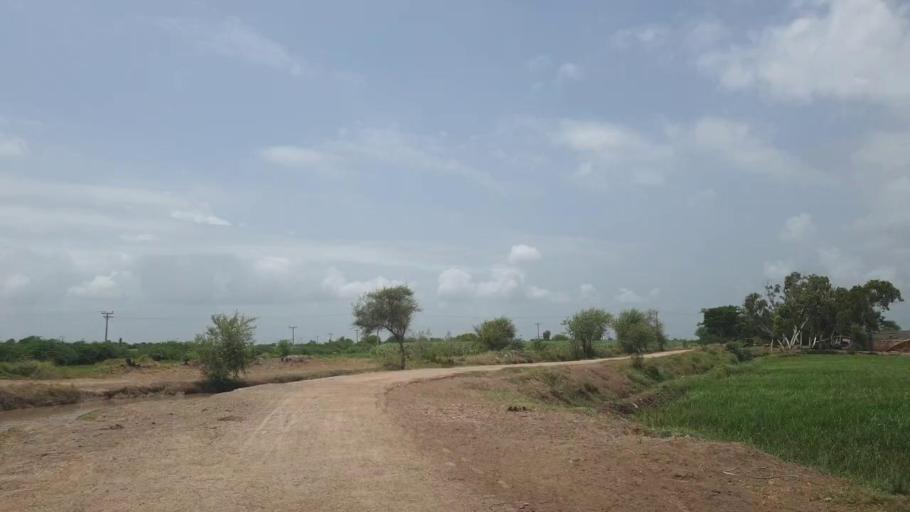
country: PK
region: Sindh
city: Badin
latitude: 24.6625
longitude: 68.9445
